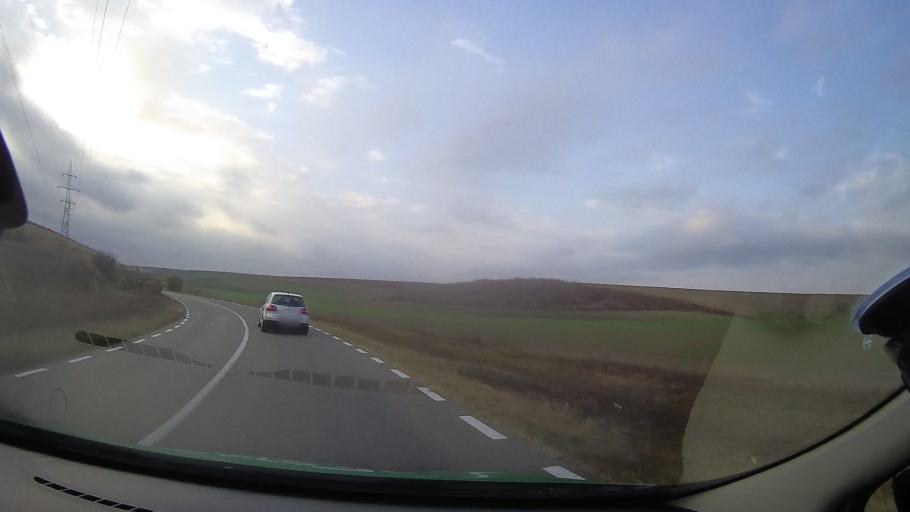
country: RO
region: Constanta
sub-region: Comuna Pestera
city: Pestera
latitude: 44.2034
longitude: 28.1506
